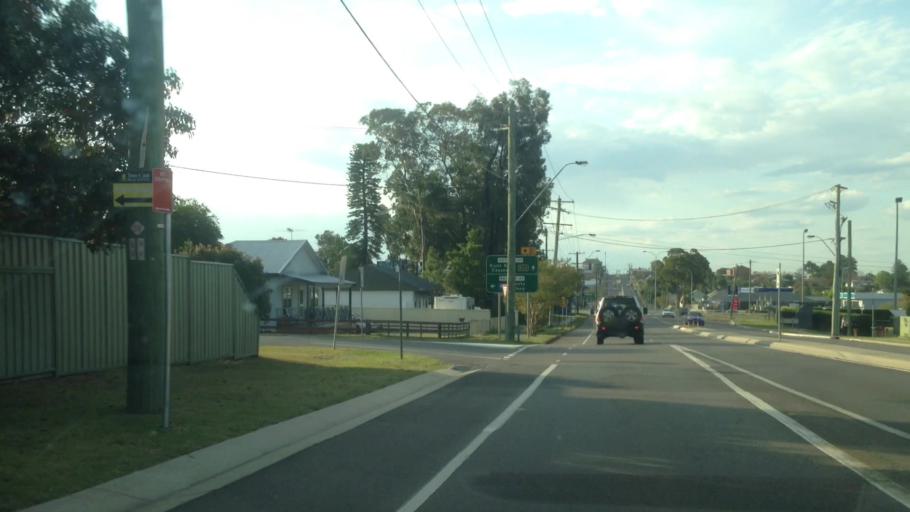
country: AU
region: New South Wales
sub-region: Cessnock
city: Kurri Kurri
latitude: -32.8259
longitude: 151.4871
